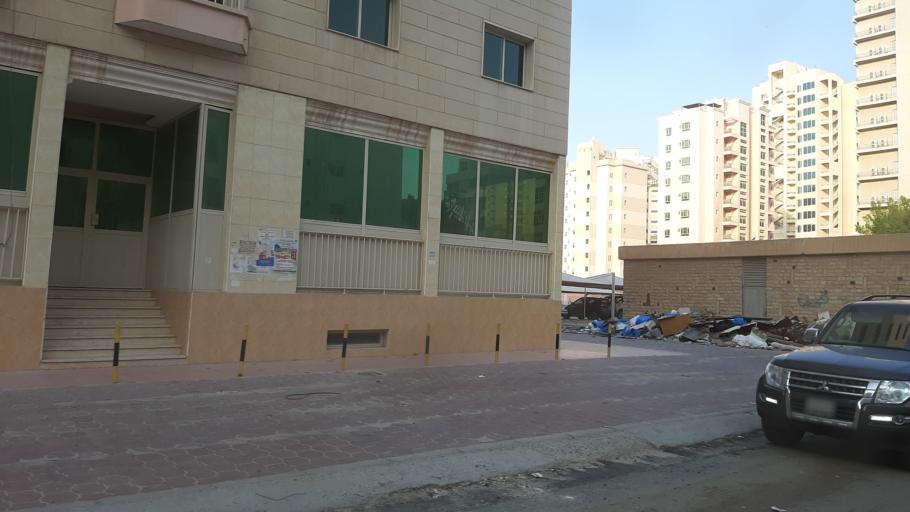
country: KW
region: Al Ahmadi
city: Al Manqaf
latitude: 29.0999
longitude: 48.1346
